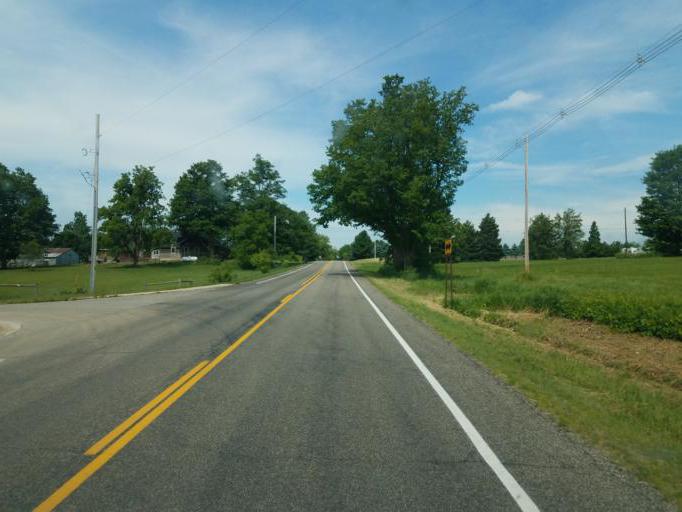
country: US
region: Michigan
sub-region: Eaton County
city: Charlotte
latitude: 42.6262
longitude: -84.8955
